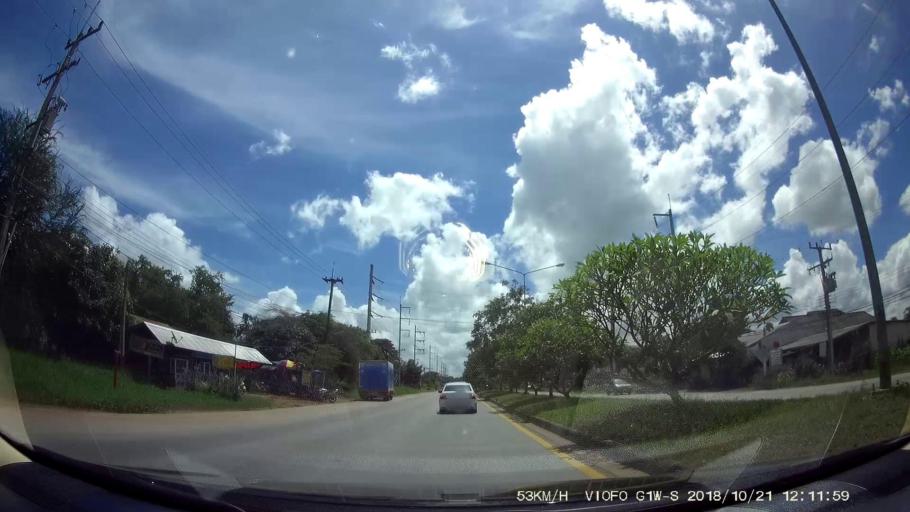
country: TH
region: Chaiyaphum
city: Chatturat
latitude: 15.4115
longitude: 101.8340
